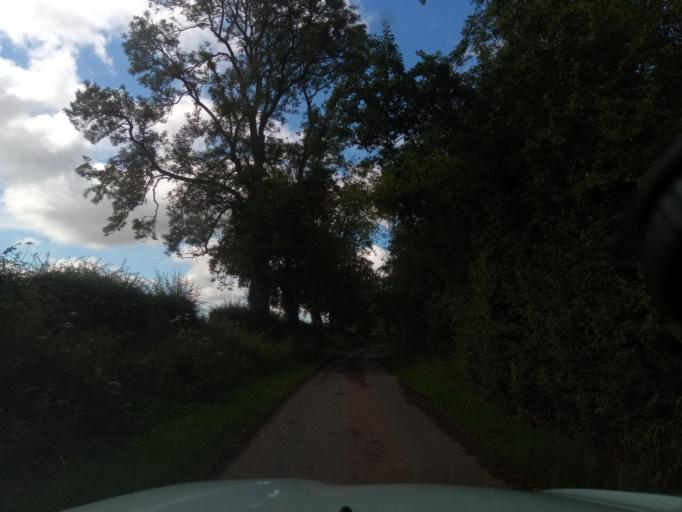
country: GB
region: Scotland
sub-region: The Scottish Borders
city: Saint Boswells
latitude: 55.5997
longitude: -2.6103
